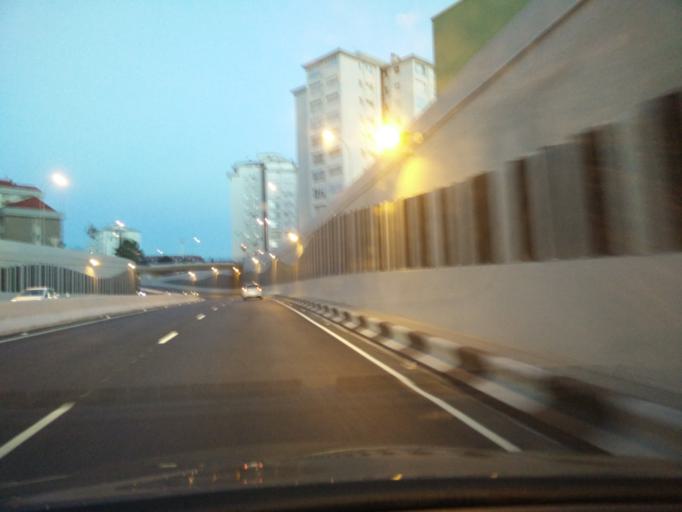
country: ES
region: Galicia
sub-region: Provincia da Coruna
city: A Coruna
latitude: 43.3443
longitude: -8.4148
